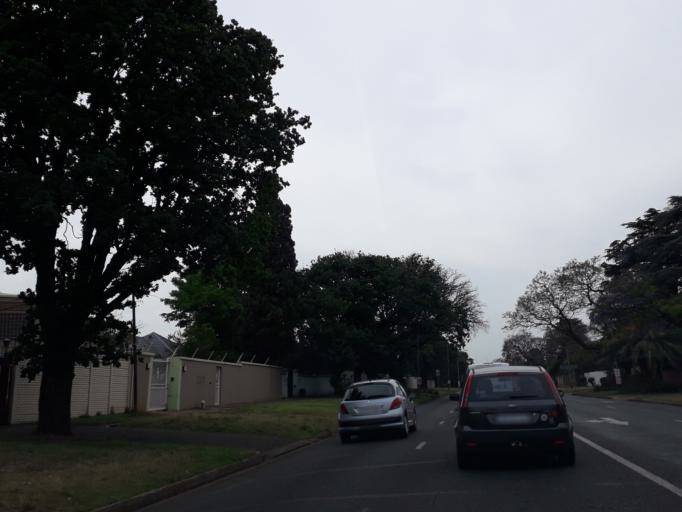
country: ZA
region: Gauteng
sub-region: City of Johannesburg Metropolitan Municipality
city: Johannesburg
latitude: -26.1548
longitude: 28.0109
